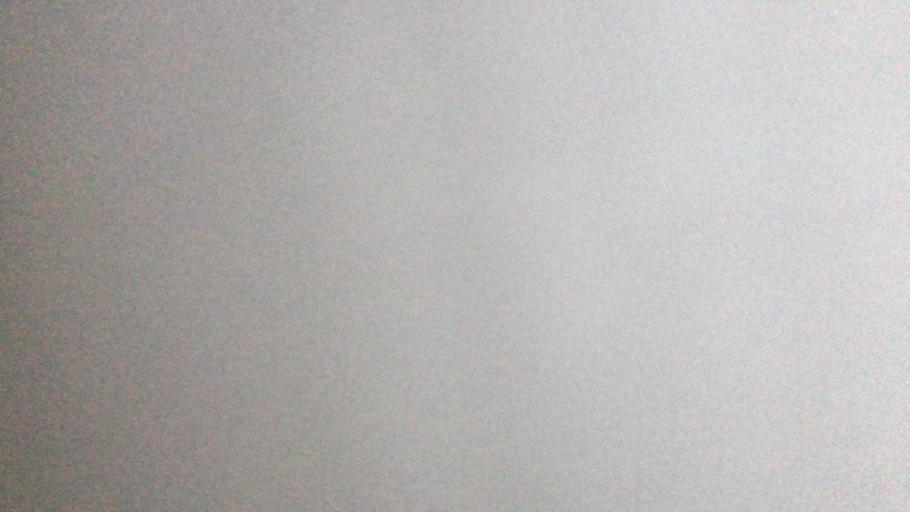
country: US
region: Washington
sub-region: King County
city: Cottage Lake
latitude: 47.7441
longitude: -122.1058
